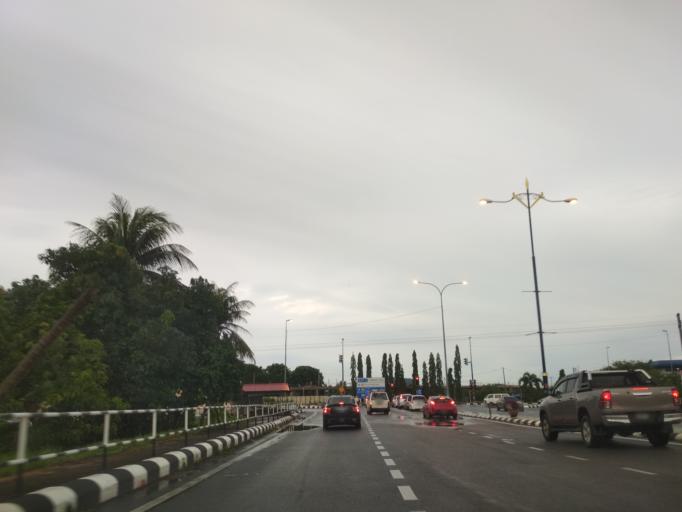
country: MY
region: Perlis
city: Kangar
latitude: 6.4386
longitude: 100.2086
